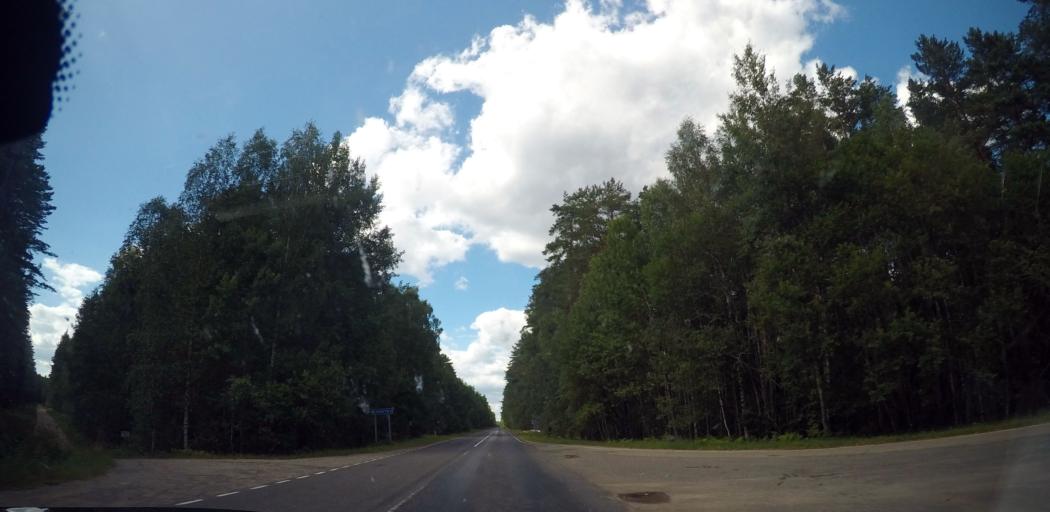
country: BY
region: Grodnenskaya
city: Skidal'
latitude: 53.8423
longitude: 24.2123
